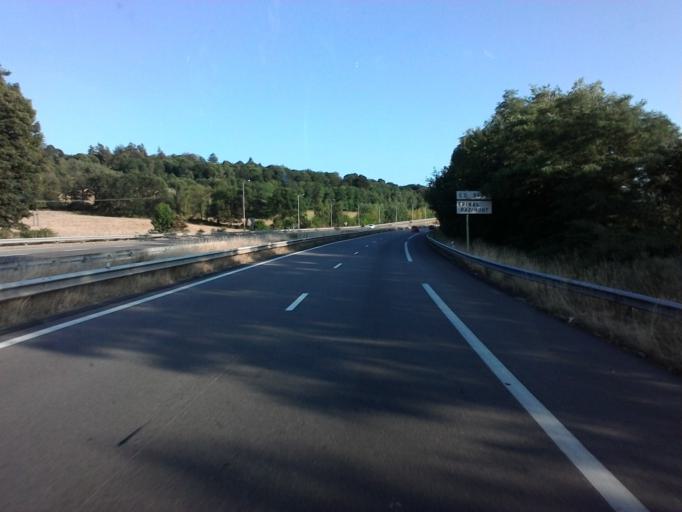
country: FR
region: Lorraine
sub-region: Departement des Vosges
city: Epinal
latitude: 48.1817
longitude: 6.4844
